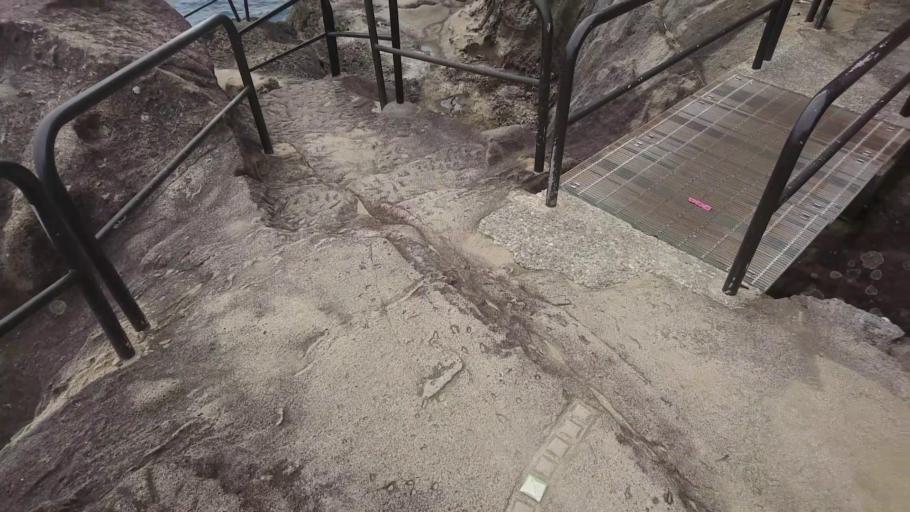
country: JP
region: Mie
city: Owase
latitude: 33.8901
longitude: 136.1161
